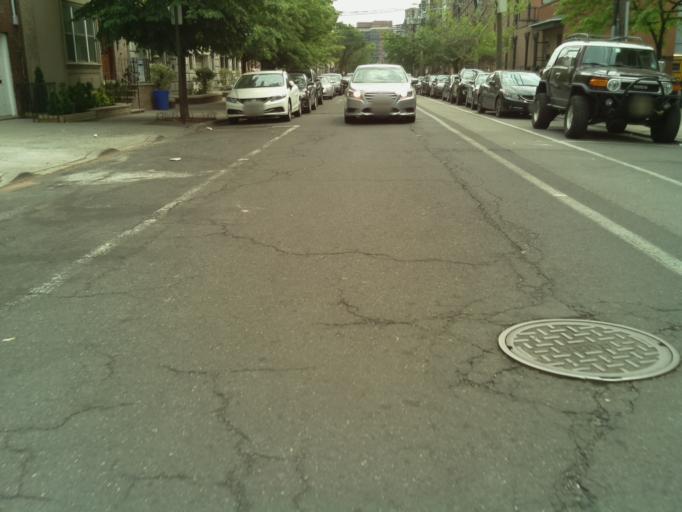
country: US
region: New Jersey
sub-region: Hudson County
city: Hoboken
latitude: 40.7408
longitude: -74.0386
